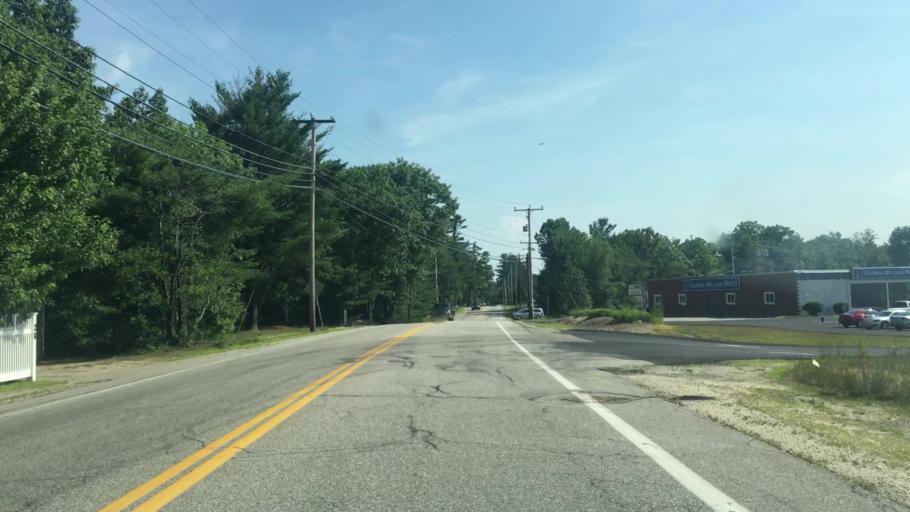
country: US
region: New Hampshire
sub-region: Strafford County
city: Rochester
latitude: 43.2880
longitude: -70.9743
